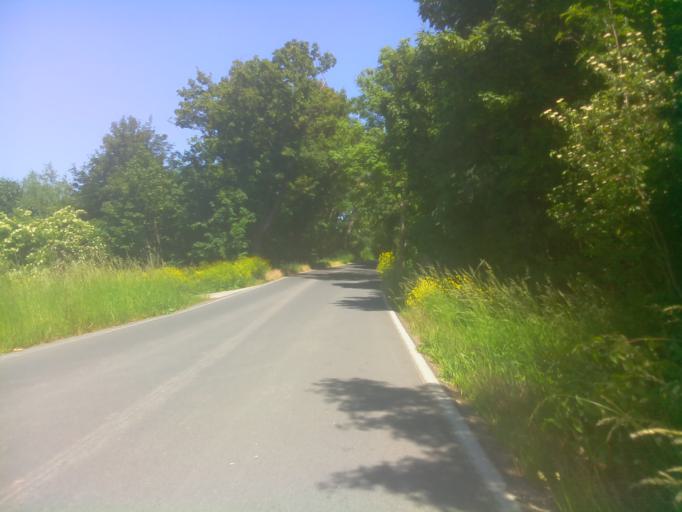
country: DE
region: Thuringia
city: Saalfeld
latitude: 50.6440
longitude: 11.3767
